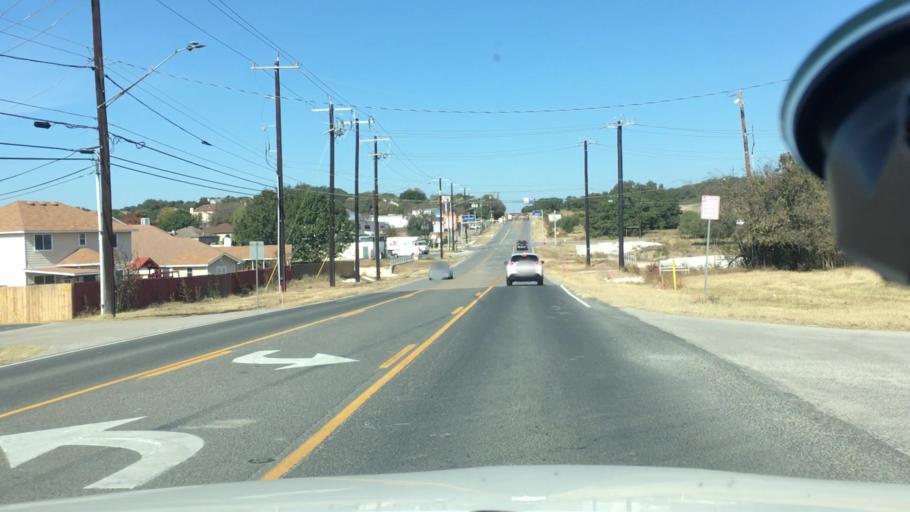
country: US
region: Texas
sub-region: Bexar County
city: Hollywood Park
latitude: 29.5774
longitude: -98.4195
